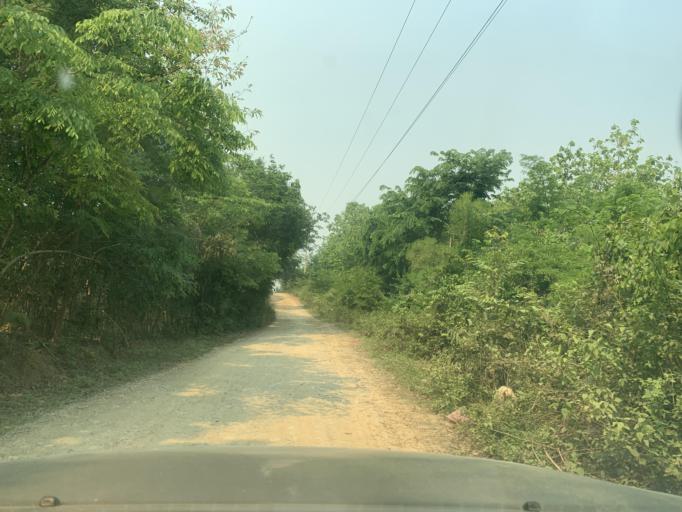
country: LA
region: Louangphabang
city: Louangphabang
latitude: 19.8939
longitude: 102.2522
